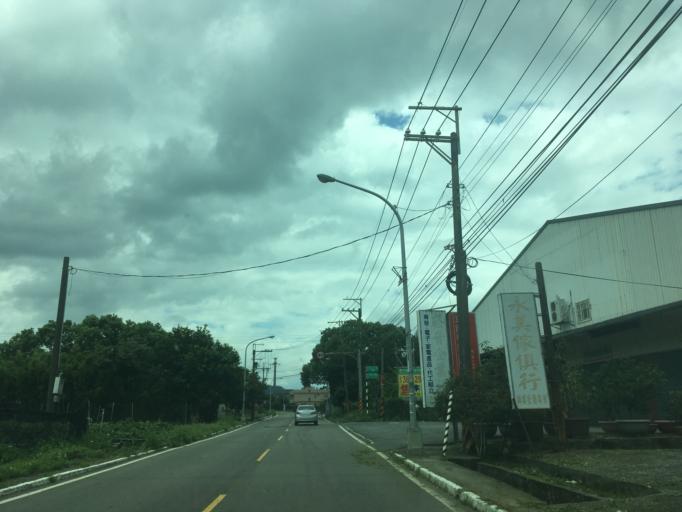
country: TW
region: Taiwan
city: Daxi
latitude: 24.8553
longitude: 121.2918
